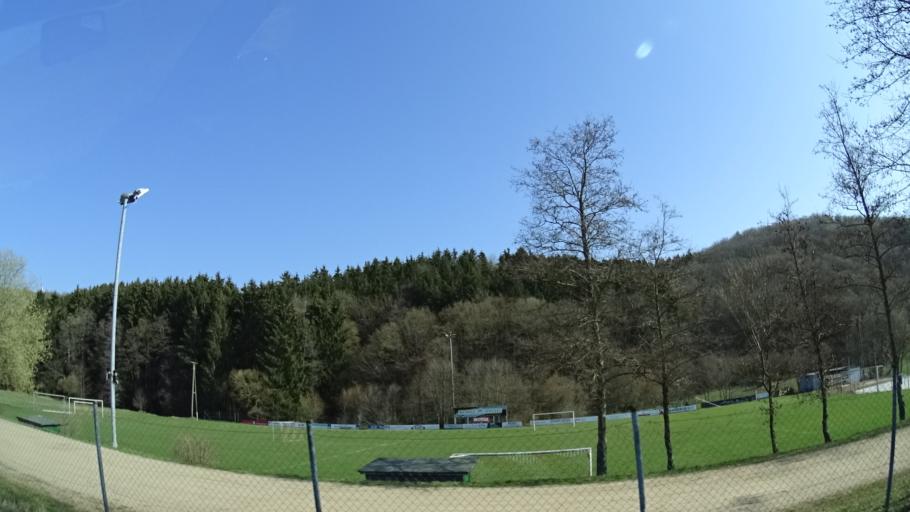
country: DE
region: Rheinland-Pfalz
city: Niederhambach
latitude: 49.6810
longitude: 7.2132
